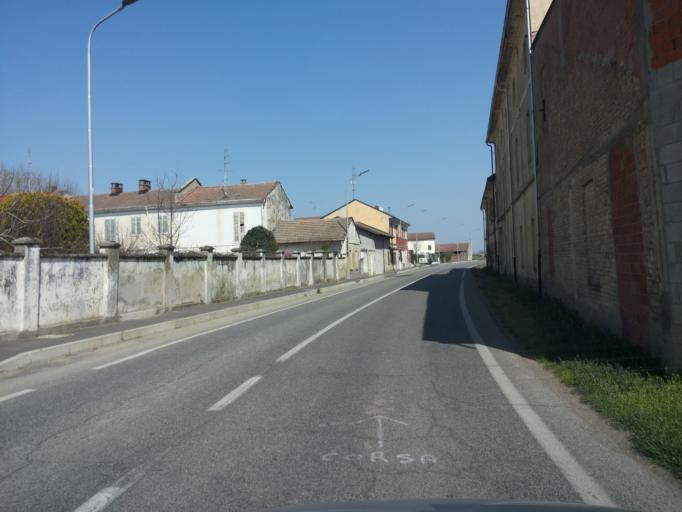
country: IT
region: Piedmont
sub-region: Provincia di Vercelli
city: Asigliano Vercellese
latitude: 45.2640
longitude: 8.4131
